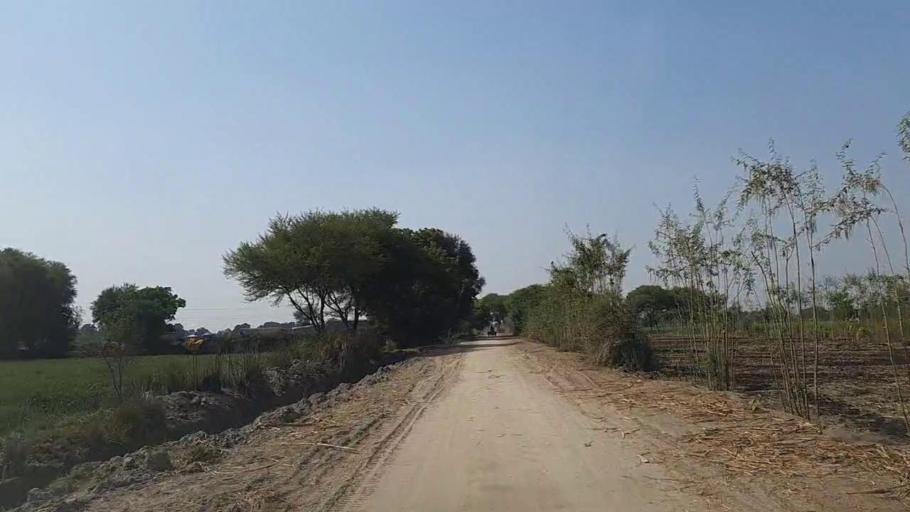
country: PK
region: Sindh
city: Nawabshah
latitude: 26.2449
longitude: 68.4700
